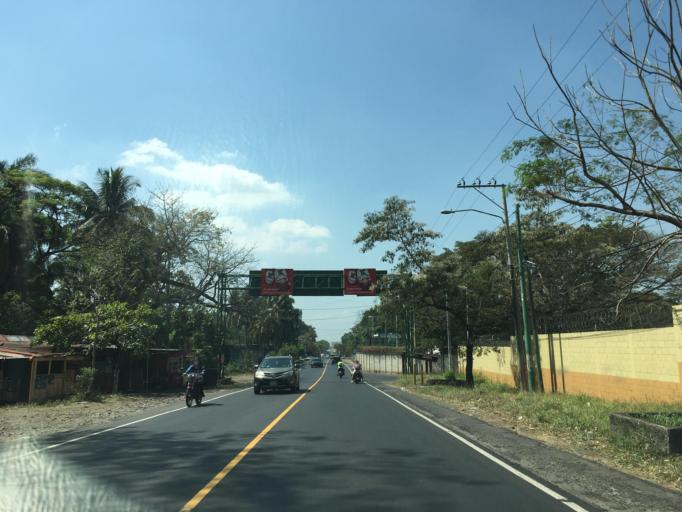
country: GT
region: Escuintla
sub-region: Municipio de Escuintla
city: Escuintla
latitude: 14.3006
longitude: -90.7927
